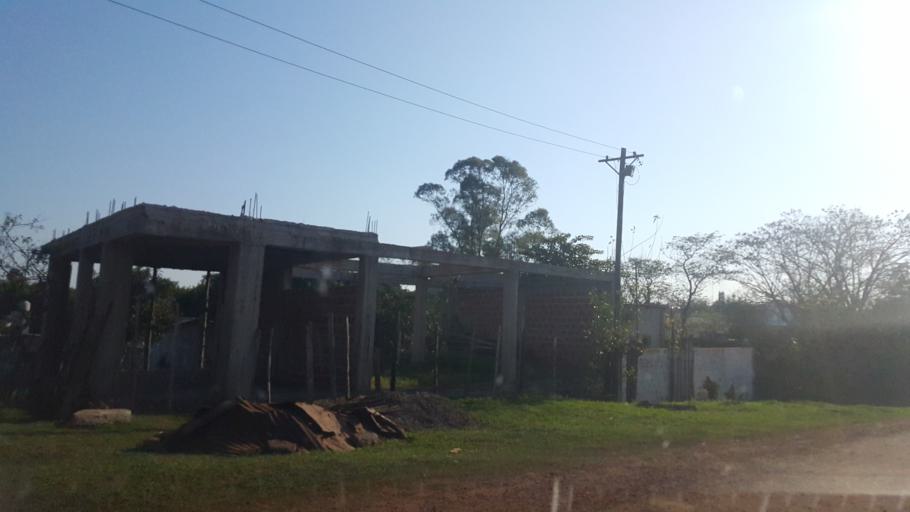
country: AR
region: Misiones
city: Garupa
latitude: -27.4527
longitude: -55.8556
